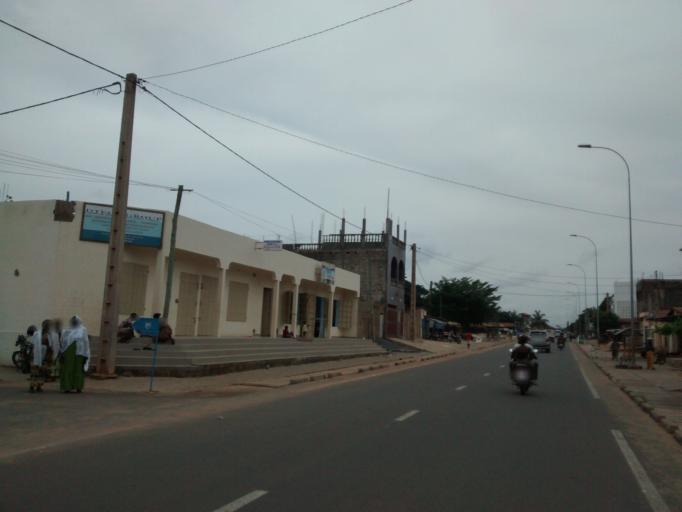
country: TG
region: Maritime
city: Lome
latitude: 6.2092
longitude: 1.1869
